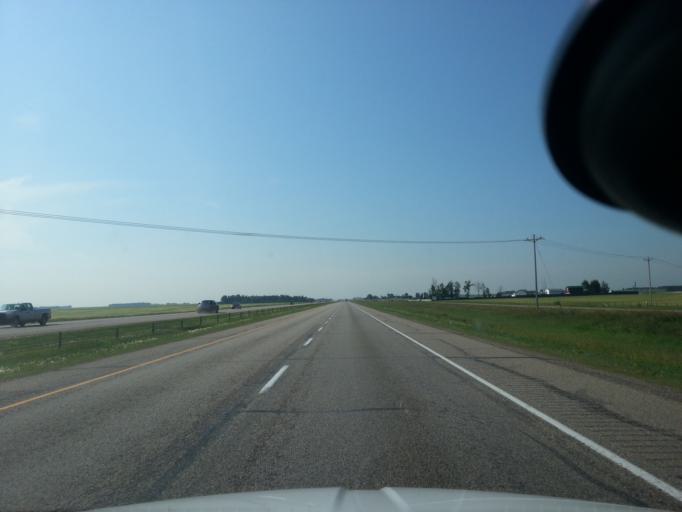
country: CA
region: Alberta
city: Olds
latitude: 51.8467
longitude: -114.0257
